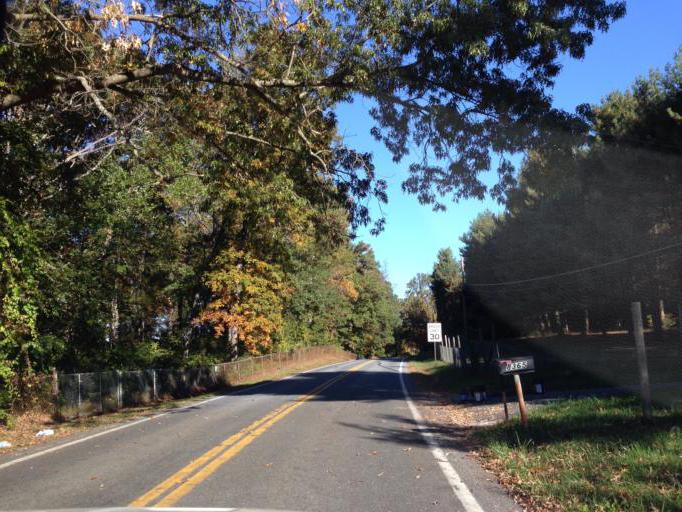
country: US
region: Maryland
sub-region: Howard County
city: Fulton
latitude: 39.1405
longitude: -76.9172
